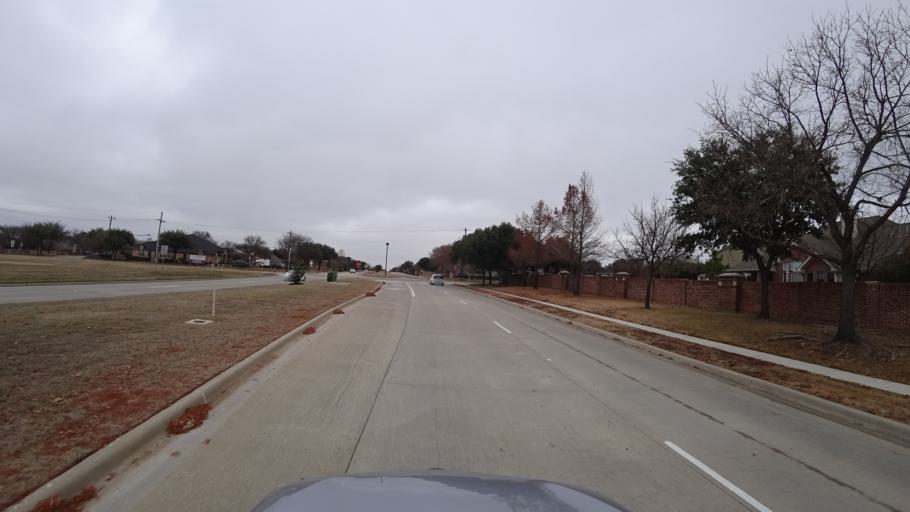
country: US
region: Texas
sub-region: Denton County
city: Lewisville
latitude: 33.0215
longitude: -97.0368
